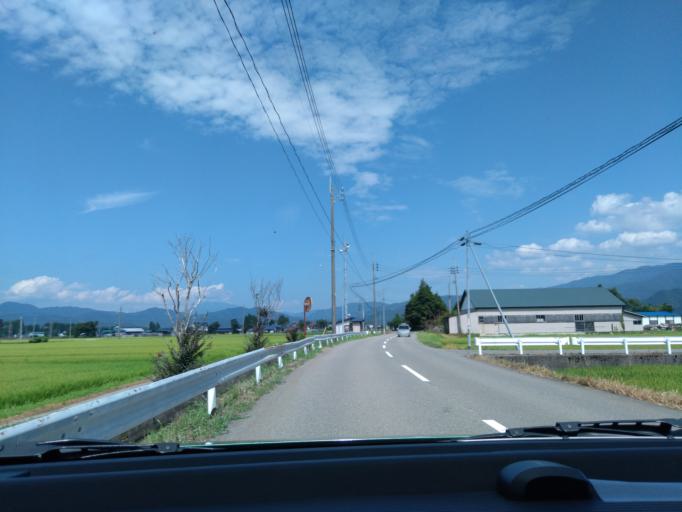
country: JP
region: Akita
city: Kakunodatemachi
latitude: 39.6025
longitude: 140.5854
